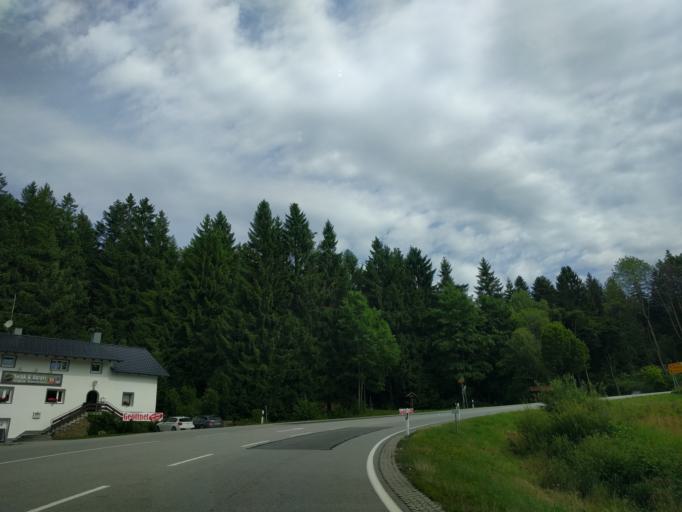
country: DE
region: Bavaria
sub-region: Lower Bavaria
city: Schaufling
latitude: 48.8755
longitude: 13.0480
